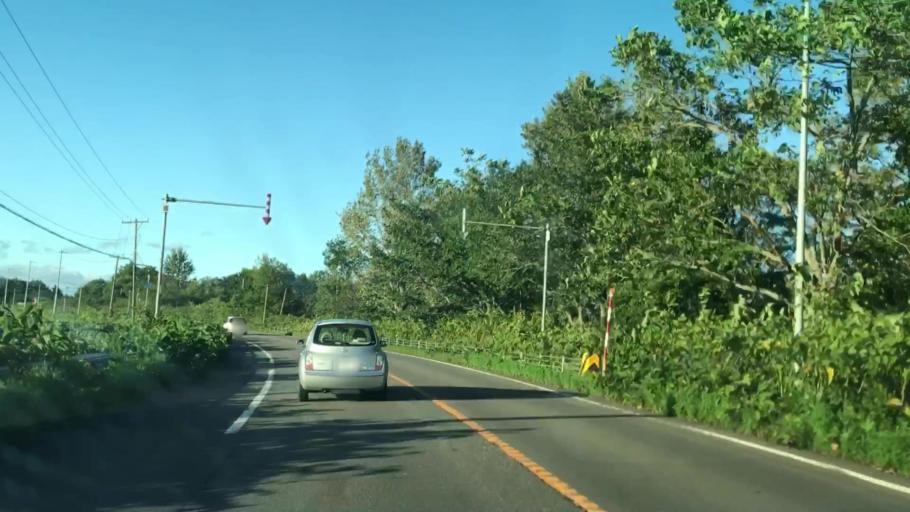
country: JP
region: Hokkaido
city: Date
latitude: 42.6494
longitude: 140.8107
